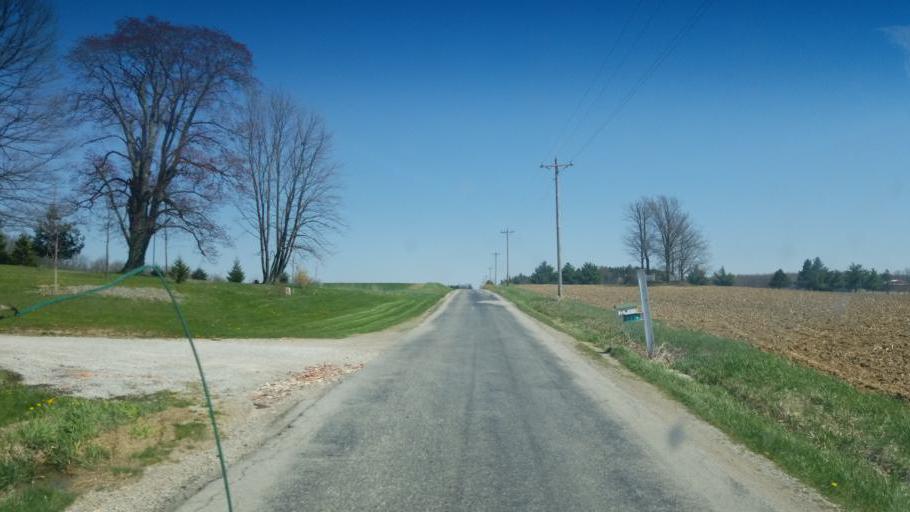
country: US
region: Ohio
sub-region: Huron County
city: Greenwich
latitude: 41.0479
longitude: -82.5035
